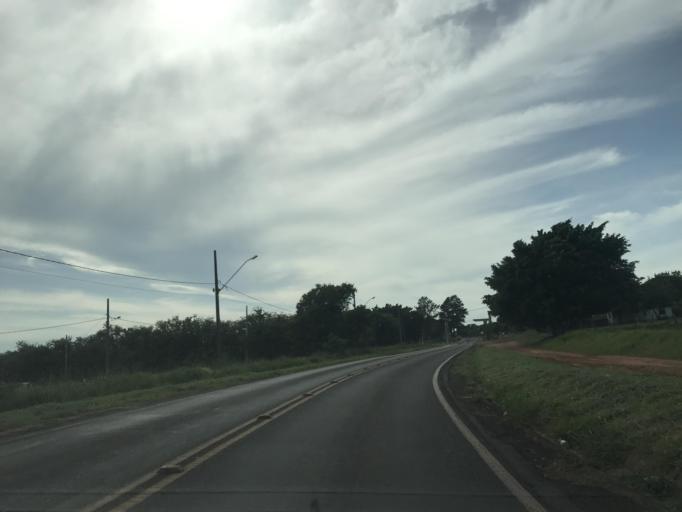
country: BR
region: Parana
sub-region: Paranavai
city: Nova Aurora
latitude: -22.9433
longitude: -52.6952
